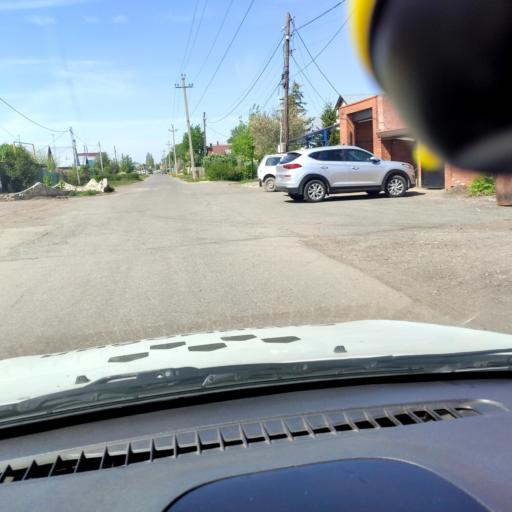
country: RU
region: Samara
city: Tol'yatti
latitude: 53.5724
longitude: 49.3223
